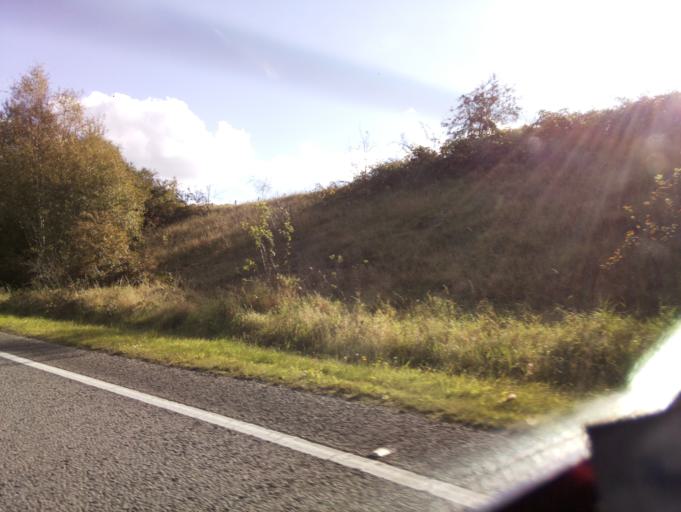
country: GB
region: Wales
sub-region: Merthyr Tydfil County Borough
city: Merthyr Tydfil
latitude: 51.7380
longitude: -3.3825
